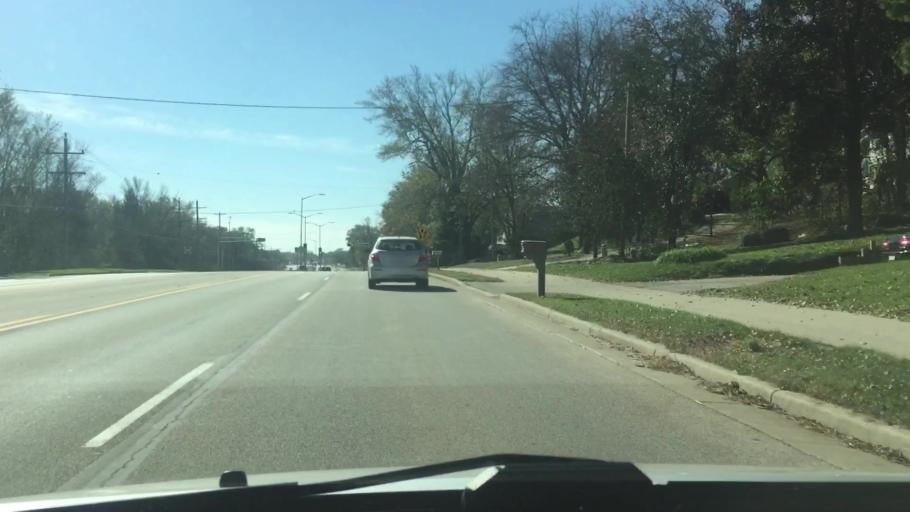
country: US
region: Wisconsin
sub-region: Waukesha County
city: Waukesha
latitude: 42.9949
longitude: -88.2616
